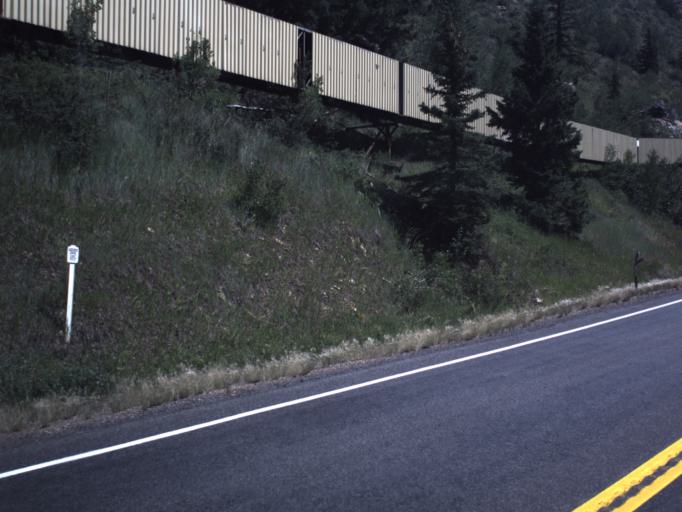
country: US
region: Utah
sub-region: Sanpete County
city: Fairview
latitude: 39.6827
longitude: -111.1733
